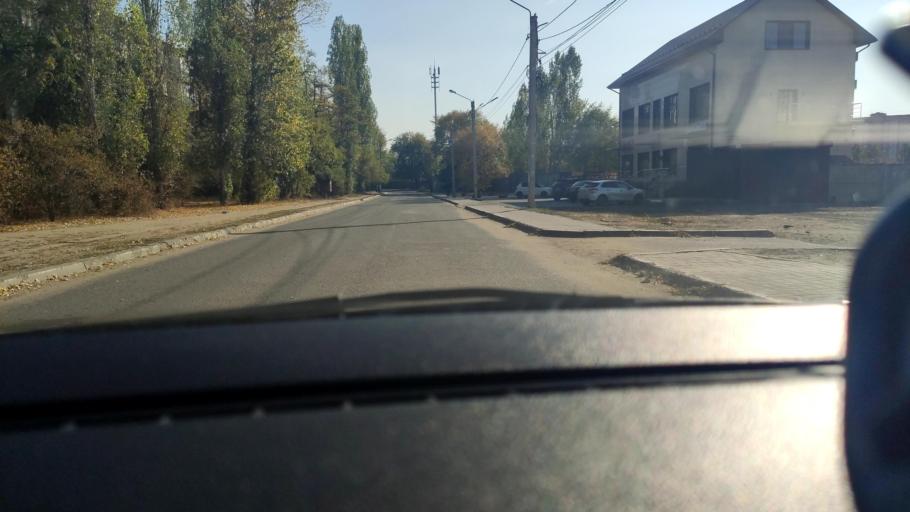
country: RU
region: Voronezj
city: Pridonskoy
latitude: 51.6253
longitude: 39.0686
